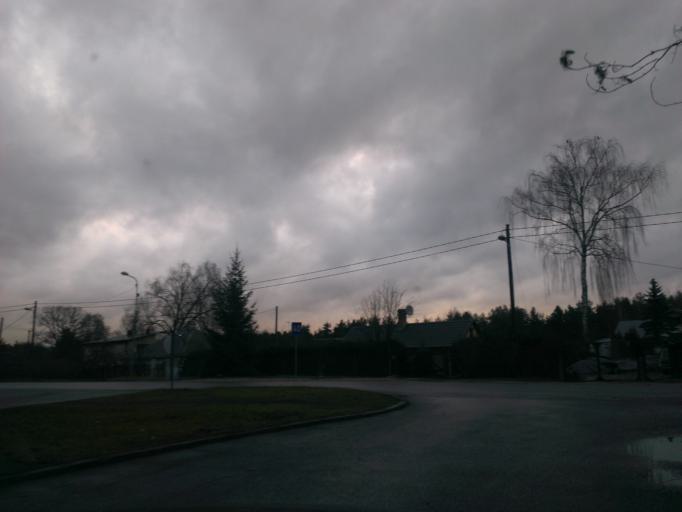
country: LV
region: Riga
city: Bergi
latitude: 56.9906
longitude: 24.2909
